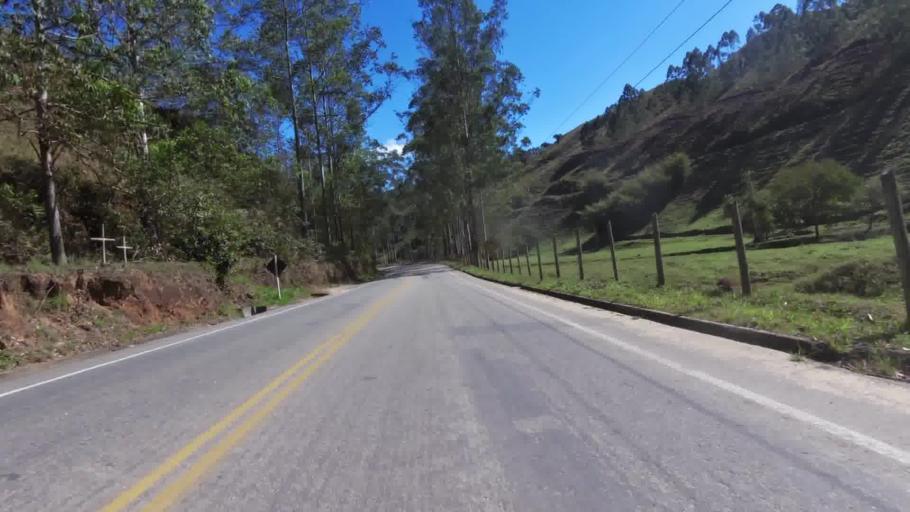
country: BR
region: Espirito Santo
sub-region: Vargem Alta
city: Vargem Alta
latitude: -20.6602
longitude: -40.9681
